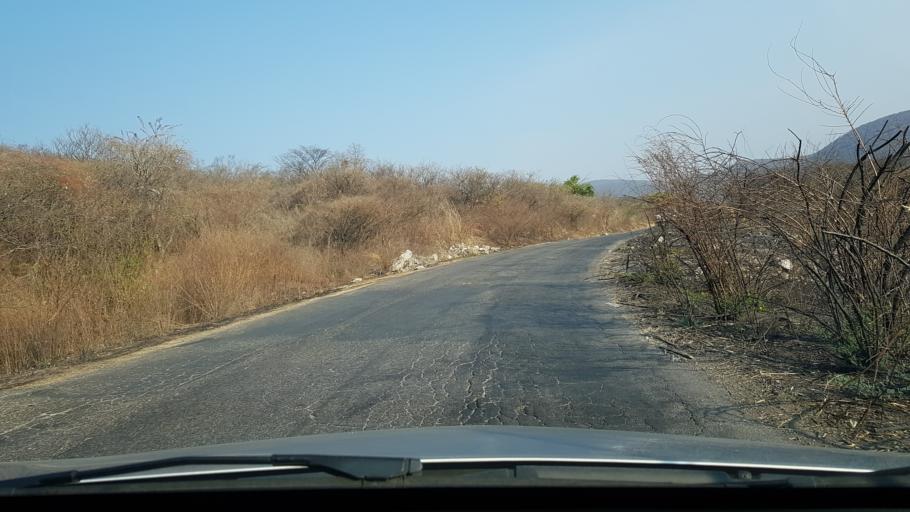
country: MX
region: Morelos
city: Tlaltizapan
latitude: 18.6646
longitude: -99.0515
